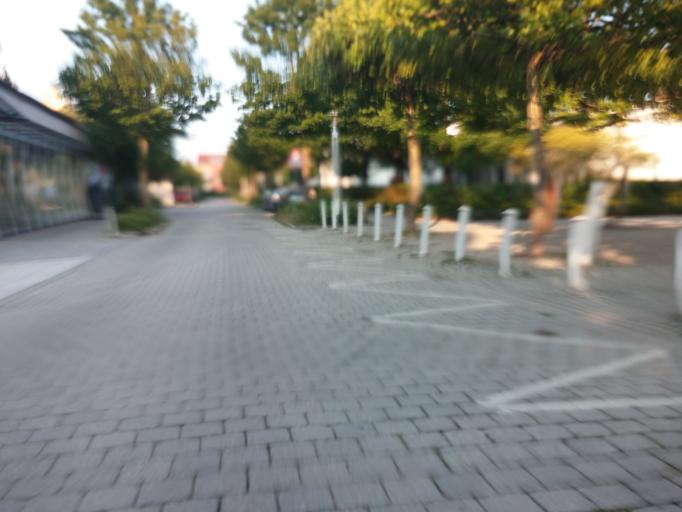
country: DE
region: Bavaria
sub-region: Upper Bavaria
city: Kirchheim bei Muenchen
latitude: 48.1618
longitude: 11.7574
